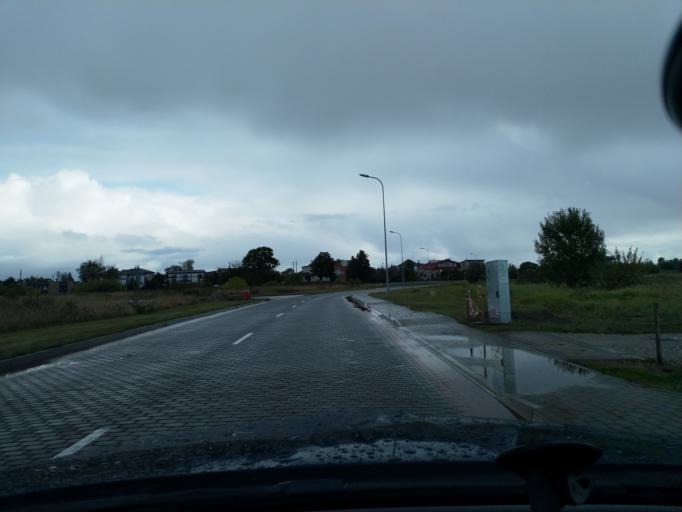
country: LV
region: Ventspils
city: Ventspils
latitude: 57.3700
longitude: 21.5833
